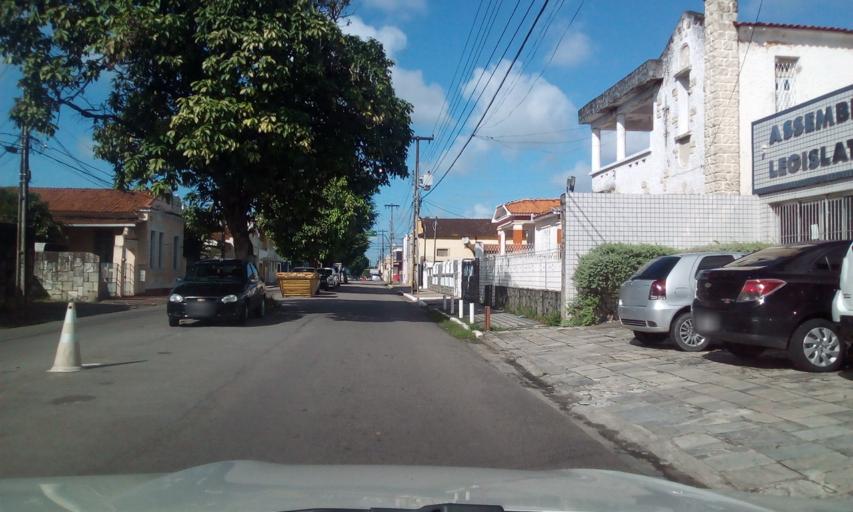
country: BR
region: Paraiba
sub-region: Joao Pessoa
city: Joao Pessoa
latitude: -7.1302
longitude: -34.8816
